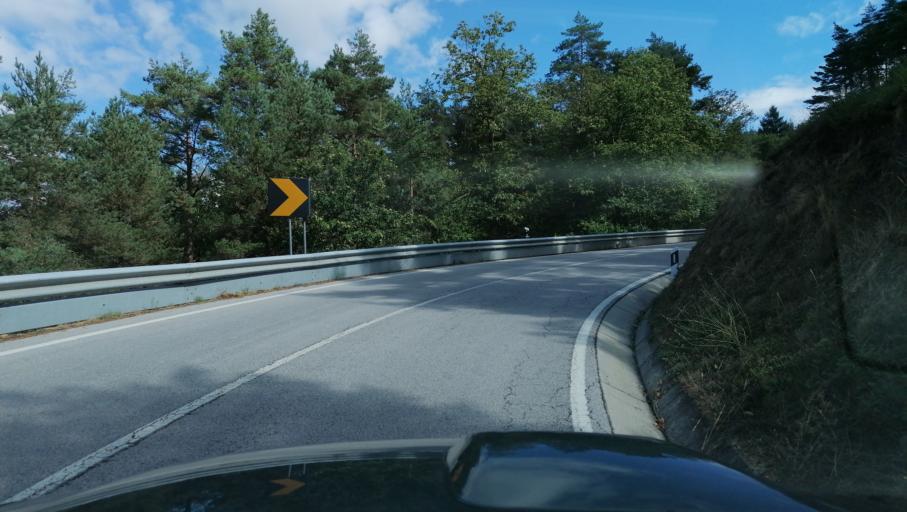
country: PT
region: Vila Real
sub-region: Vila Pouca de Aguiar
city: Vila Pouca de Aguiar
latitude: 41.5124
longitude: -7.6119
